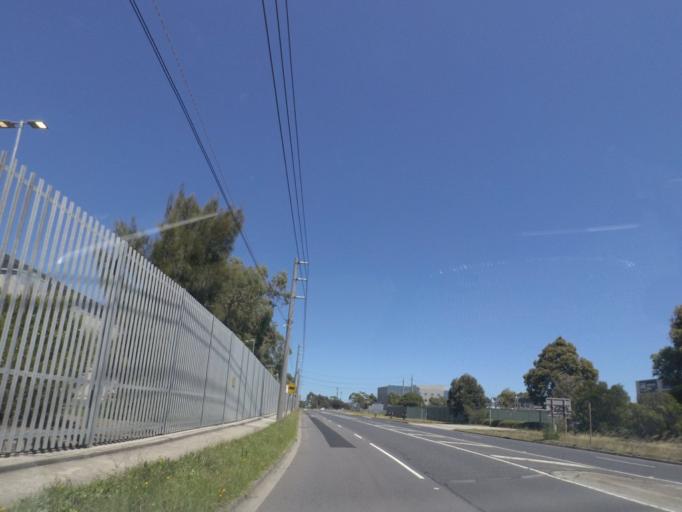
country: AU
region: Victoria
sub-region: Maribyrnong
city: Yarraville
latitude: -37.8236
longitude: 144.9111
